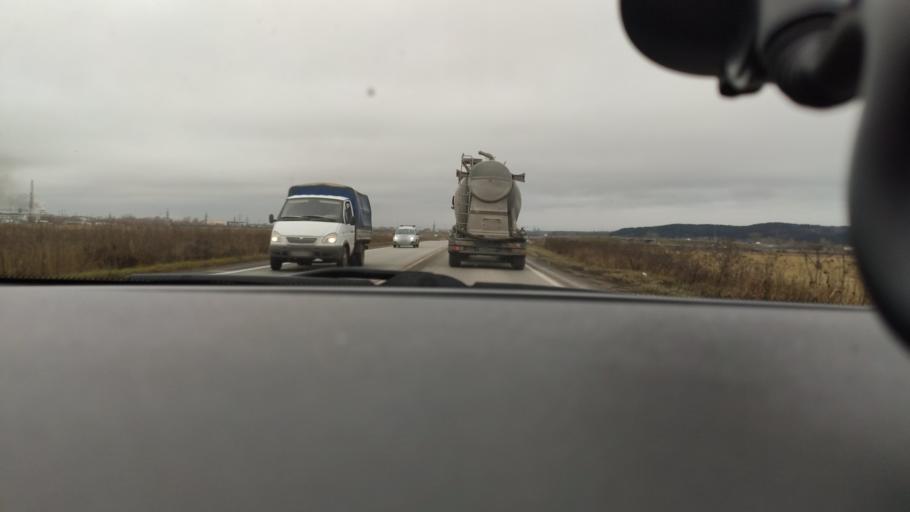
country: RU
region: Perm
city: Gamovo
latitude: 57.9214
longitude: 56.1788
